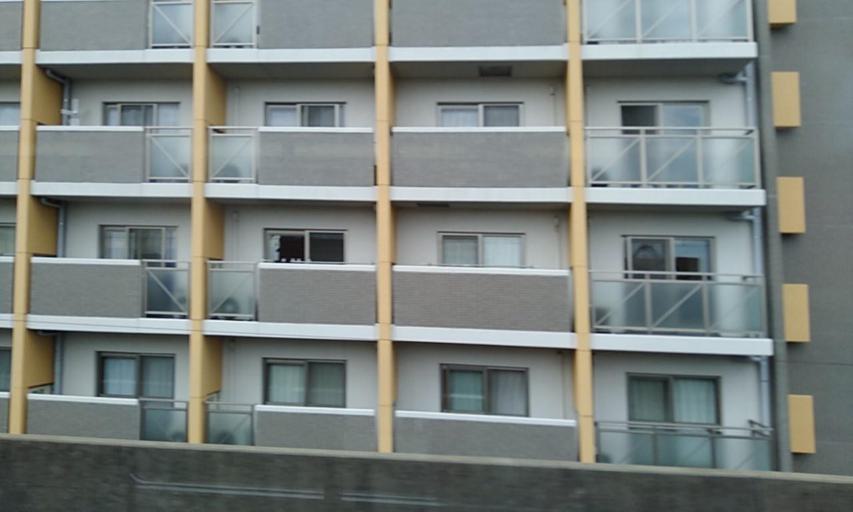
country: JP
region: Osaka
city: Osaka-shi
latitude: 34.6342
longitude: 135.5281
